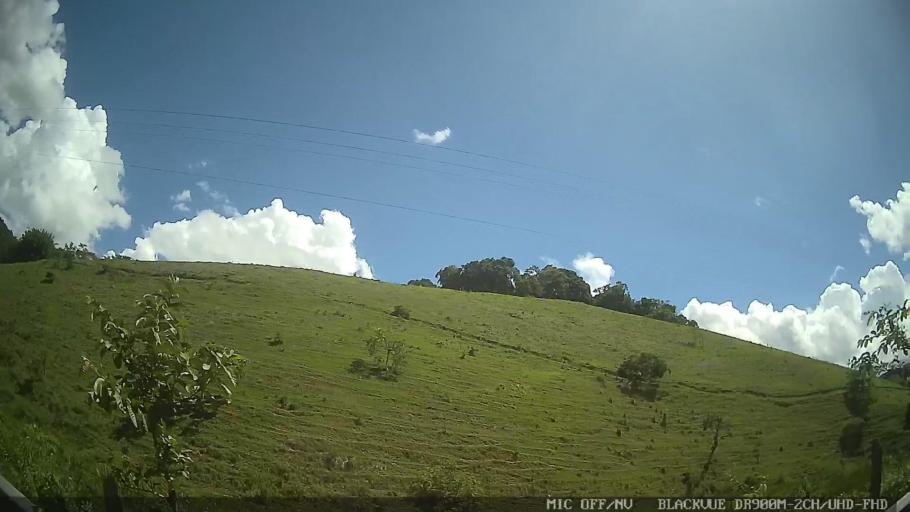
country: BR
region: Sao Paulo
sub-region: Caraguatatuba
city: Caraguatatuba
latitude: -23.5197
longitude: -45.5423
